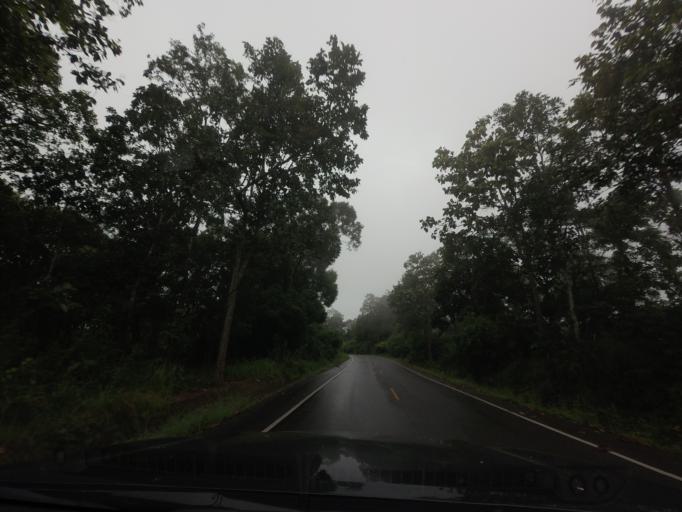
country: TH
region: Nong Khai
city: Sangkhom
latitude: 18.0384
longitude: 102.3297
